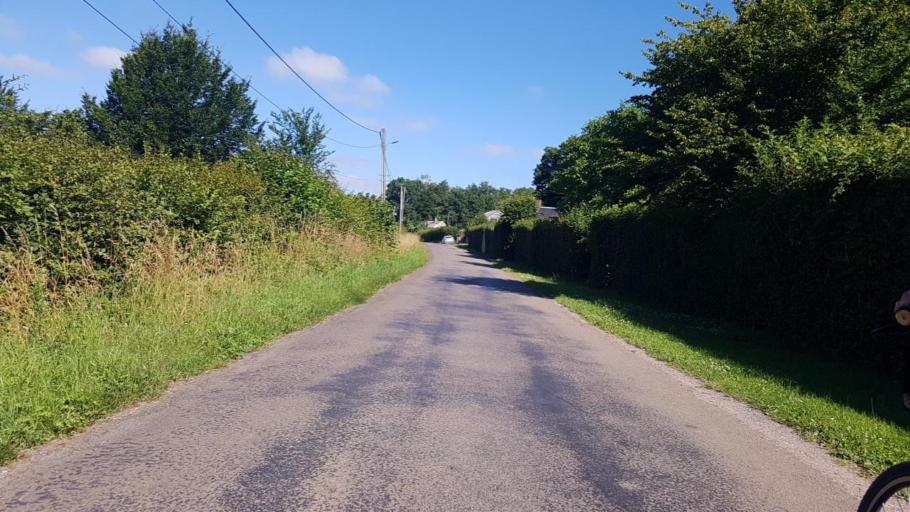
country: FR
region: Nord-Pas-de-Calais
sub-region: Departement du Nord
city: Anor
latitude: 49.9832
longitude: 4.1273
